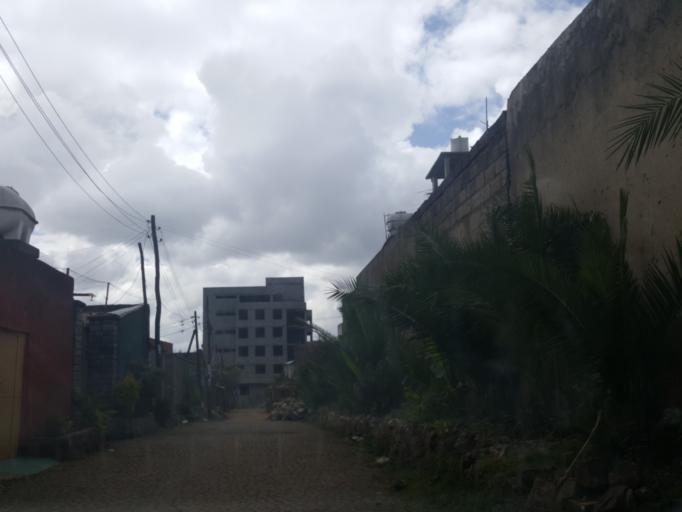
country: ET
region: Adis Abeba
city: Addis Ababa
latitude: 9.0701
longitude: 38.7371
